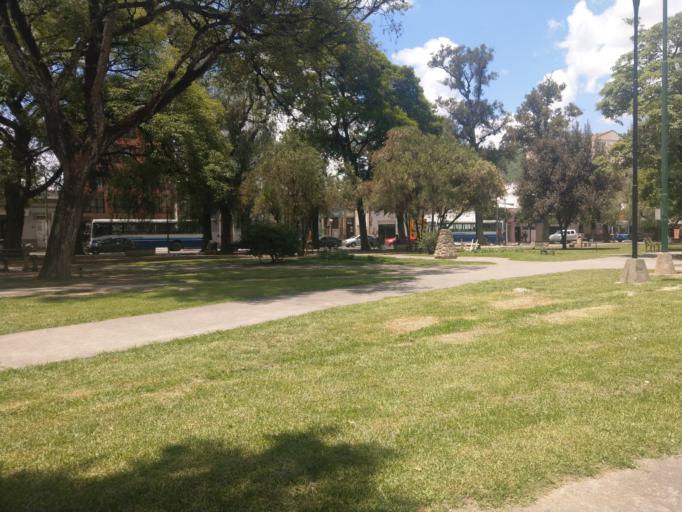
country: AR
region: Salta
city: Salta
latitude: -24.7944
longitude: -65.4068
